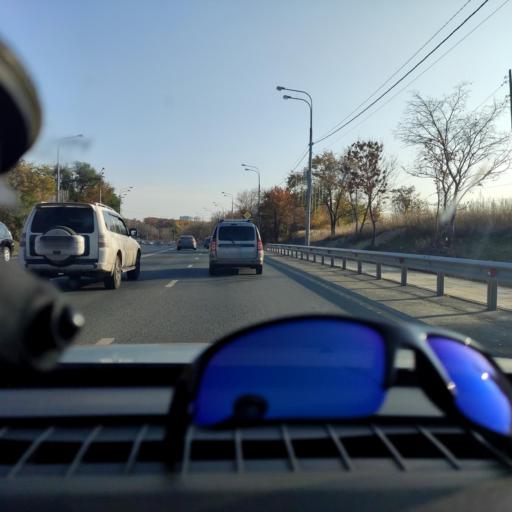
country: RU
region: Samara
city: Samara
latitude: 53.2899
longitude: 50.2241
